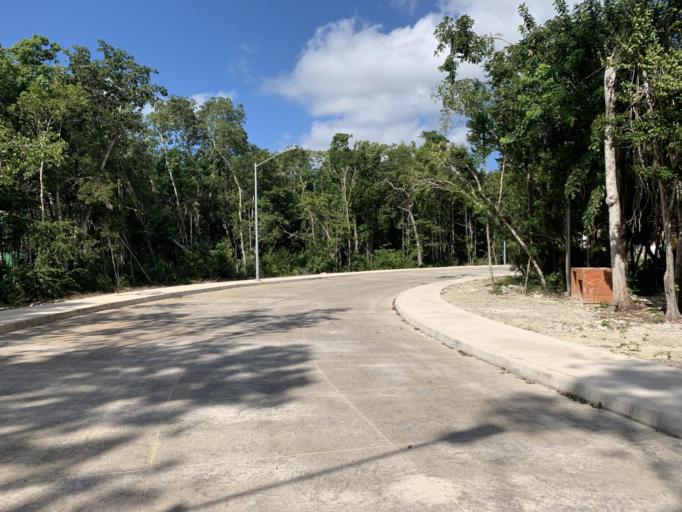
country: MX
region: Quintana Roo
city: Alfredo V. Bonfil
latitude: 20.8711
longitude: -86.9036
